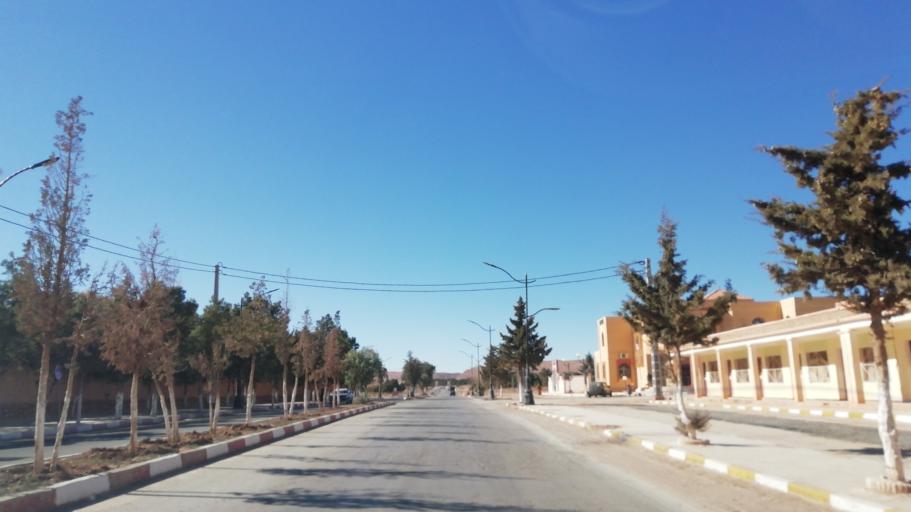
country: DZ
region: El Bayadh
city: El Bayadh
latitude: 33.7252
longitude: 1.5287
